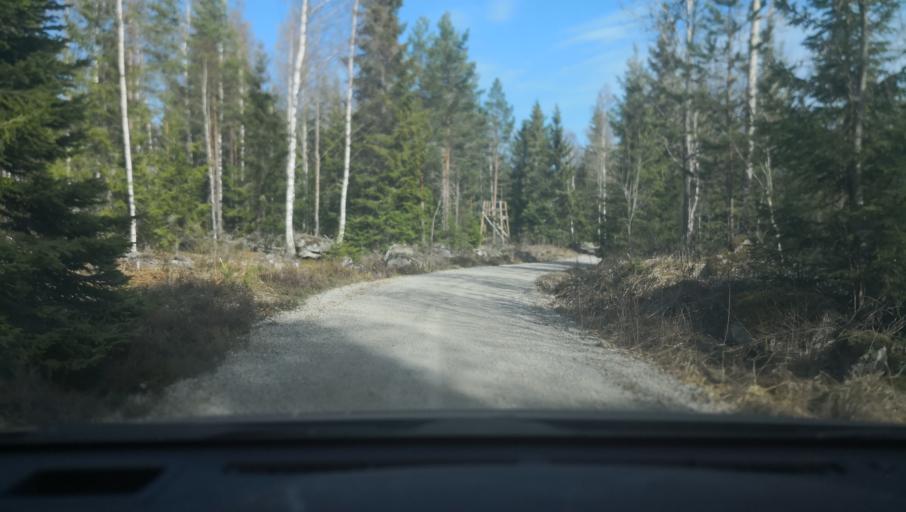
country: SE
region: Uppsala
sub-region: Heby Kommun
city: Heby
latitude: 59.8407
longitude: 16.8622
